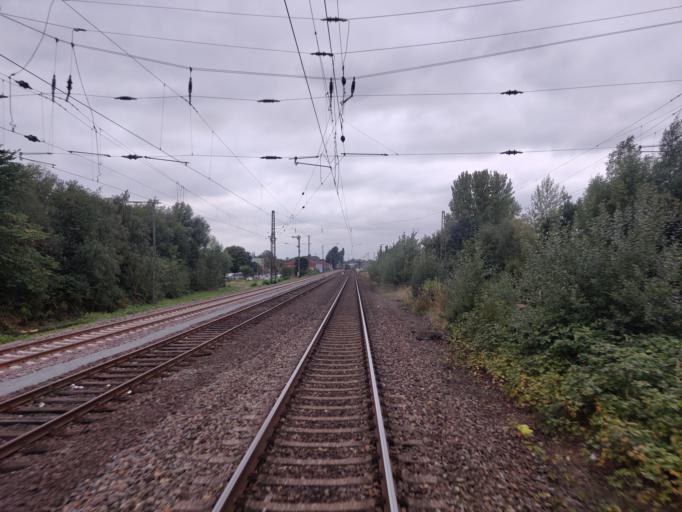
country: DE
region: Lower Saxony
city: Ritterhude
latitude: 53.1346
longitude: 8.7451
